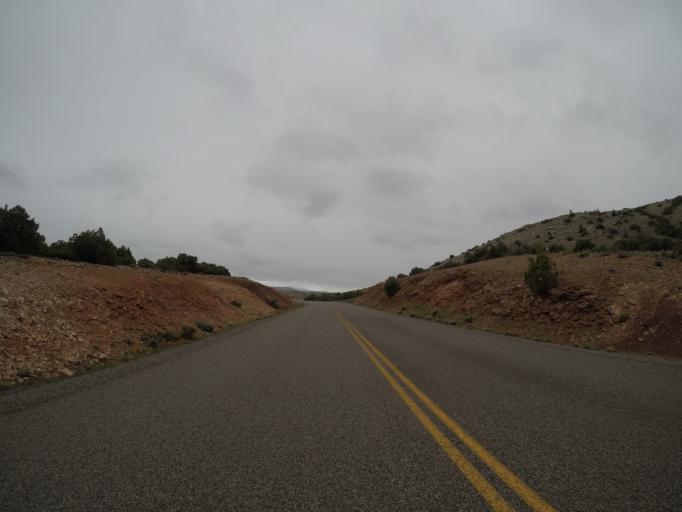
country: US
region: Wyoming
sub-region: Big Horn County
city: Lovell
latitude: 45.0238
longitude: -108.2550
